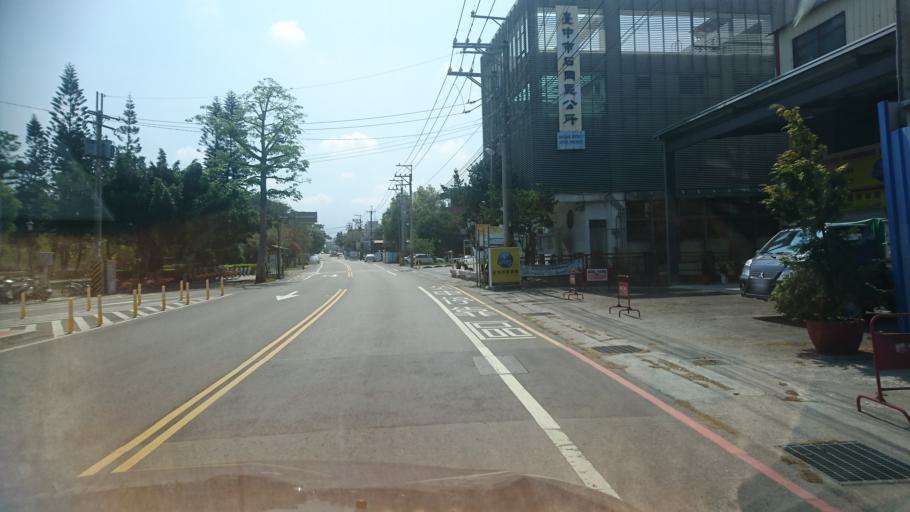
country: TW
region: Taiwan
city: Fengyuan
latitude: 24.2751
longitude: 120.7800
